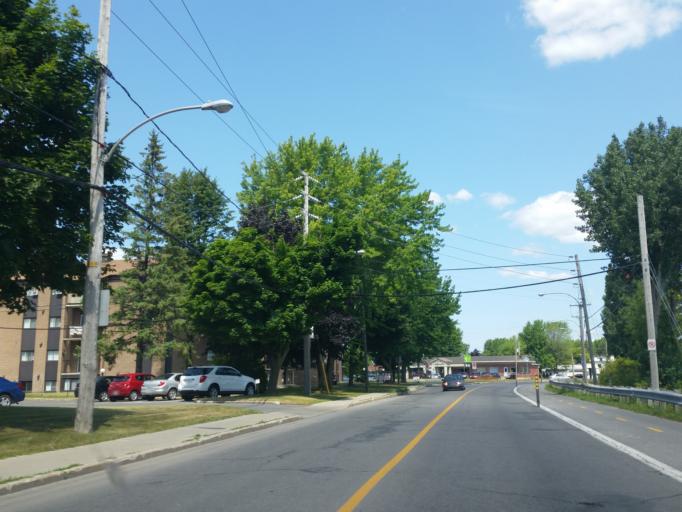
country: CA
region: Quebec
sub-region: Monteregie
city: Saint-Jean-sur-Richelieu
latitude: 45.3390
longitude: -73.2662
